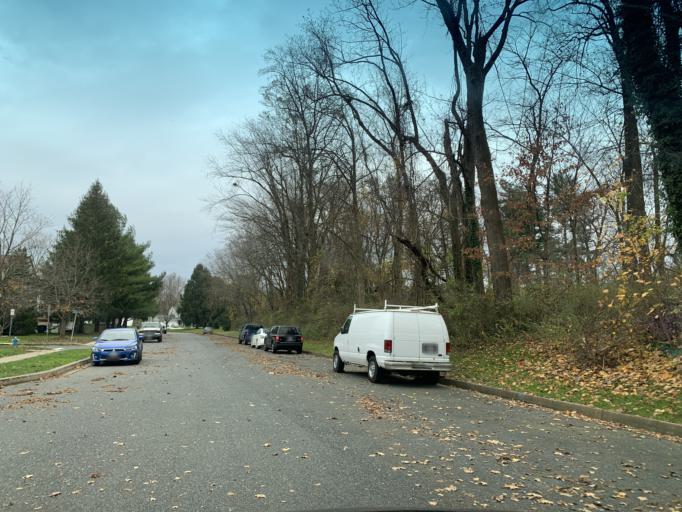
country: US
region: Maryland
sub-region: Harford County
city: North Bel Air
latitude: 39.5467
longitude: -76.3477
